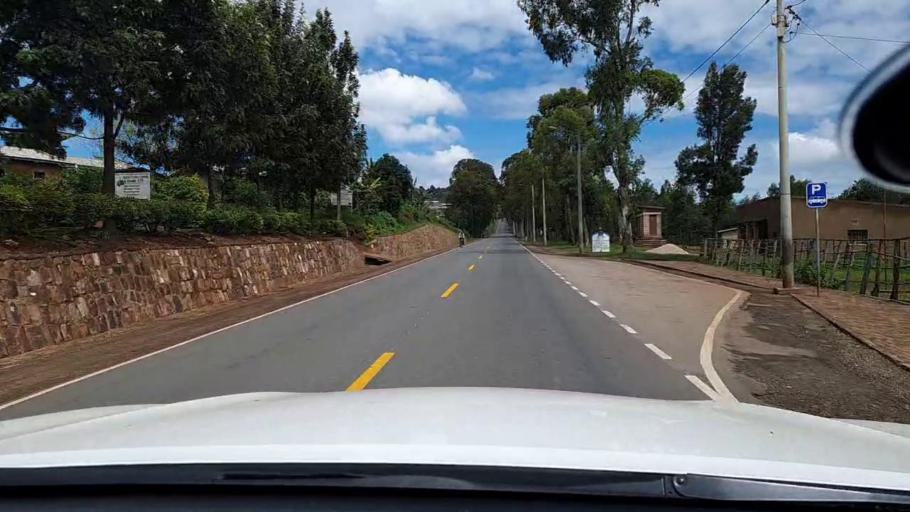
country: RW
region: Kigali
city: Kigali
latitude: -1.8354
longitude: 29.9522
